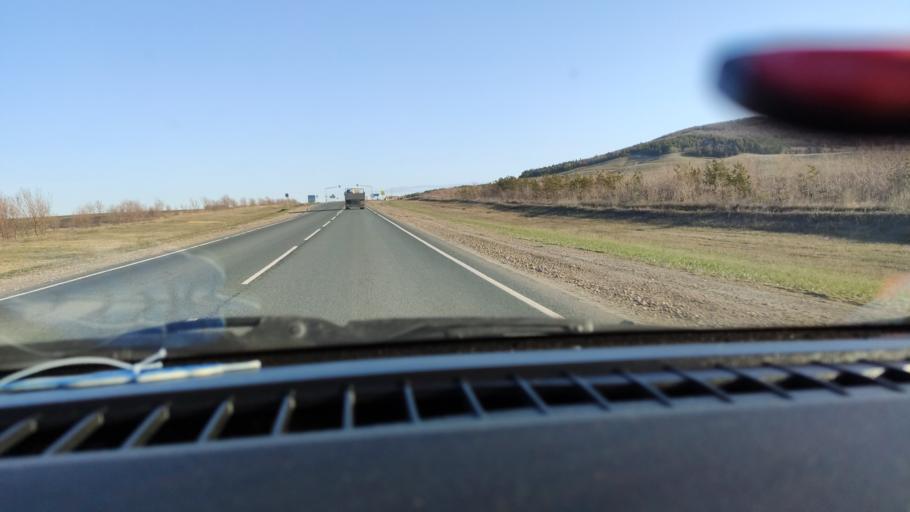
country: RU
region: Saratov
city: Alekseyevka
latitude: 52.2892
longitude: 47.9303
